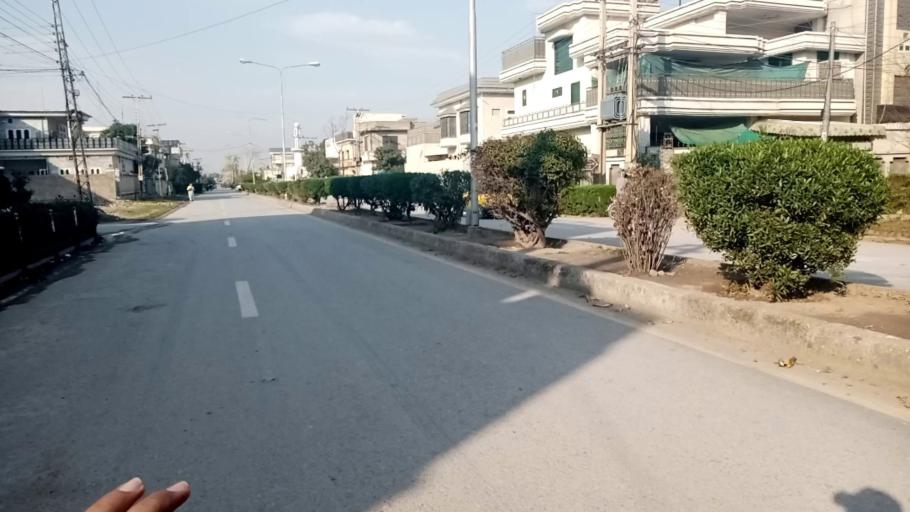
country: PK
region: Khyber Pakhtunkhwa
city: Peshawar
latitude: 33.9854
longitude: 71.4453
